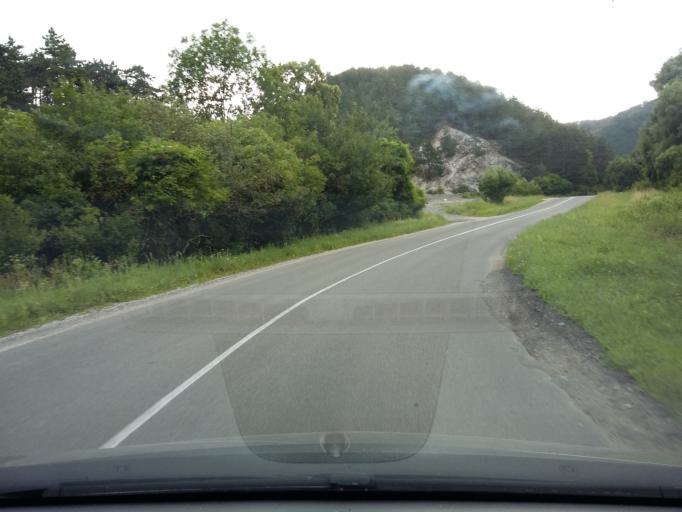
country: SK
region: Trnavsky
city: Smolenice
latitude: 48.5436
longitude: 17.4147
